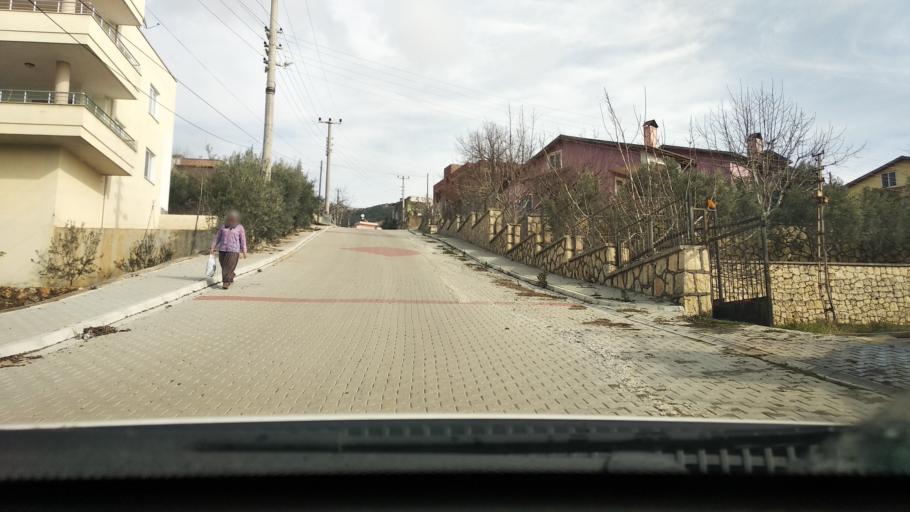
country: TR
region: Mersin
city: Kuzucubelen
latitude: 36.8762
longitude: 34.4670
